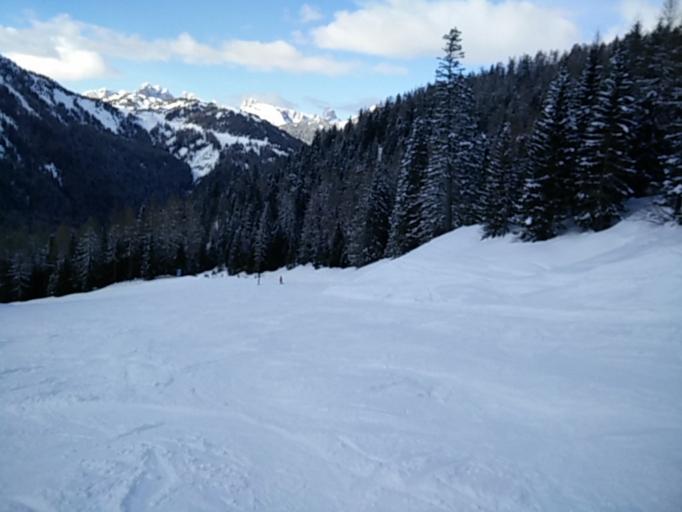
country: IT
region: Veneto
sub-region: Provincia di Belluno
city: Fusine
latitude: 46.3816
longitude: 12.0898
